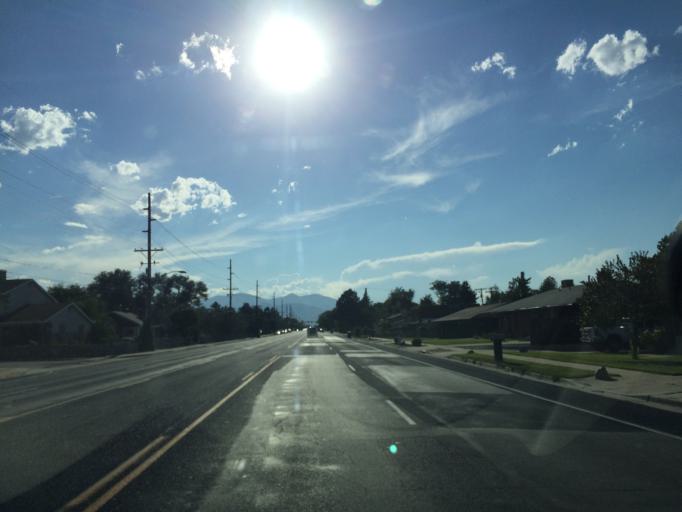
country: US
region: Utah
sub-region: Salt Lake County
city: Taylorsville
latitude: 40.6822
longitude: -111.9620
